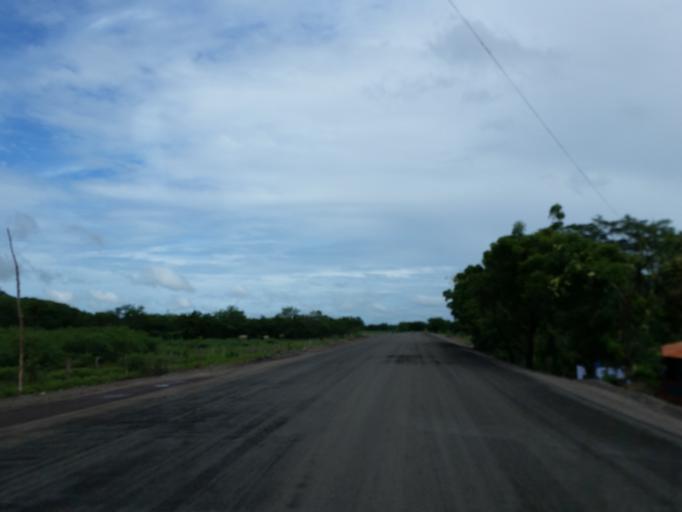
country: NI
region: Leon
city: Larreynaga
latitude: 12.5374
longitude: -86.6089
